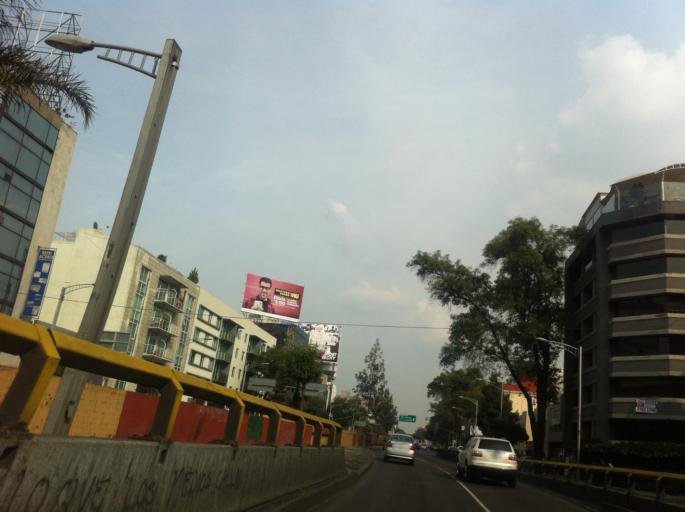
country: MX
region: Mexico City
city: Cuauhtemoc
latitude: 19.4243
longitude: -99.1604
